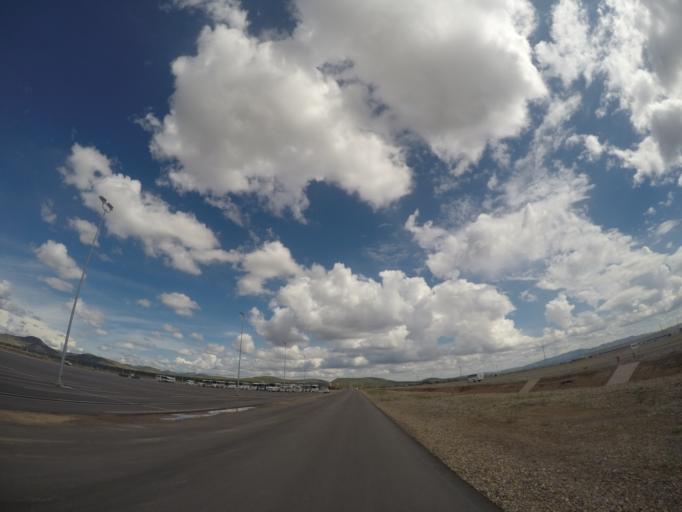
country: MX
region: San Luis Potosi
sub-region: Zaragoza
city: Cerro Gordo
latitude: 21.9662
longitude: -100.8474
